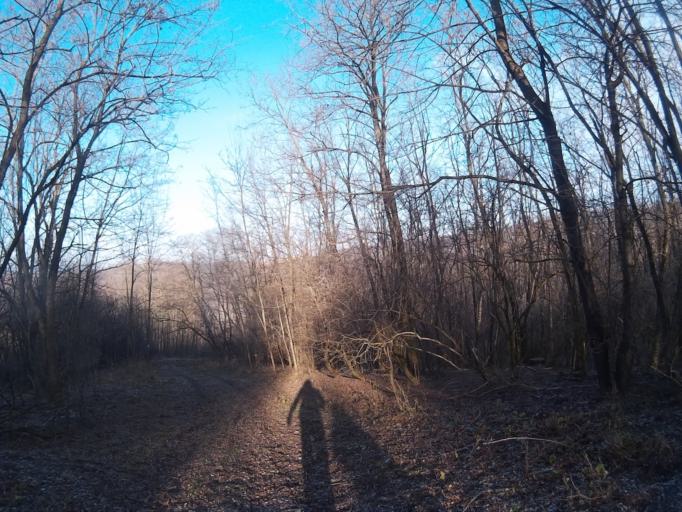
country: HU
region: Nograd
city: Bercel
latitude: 47.9545
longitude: 19.4400
